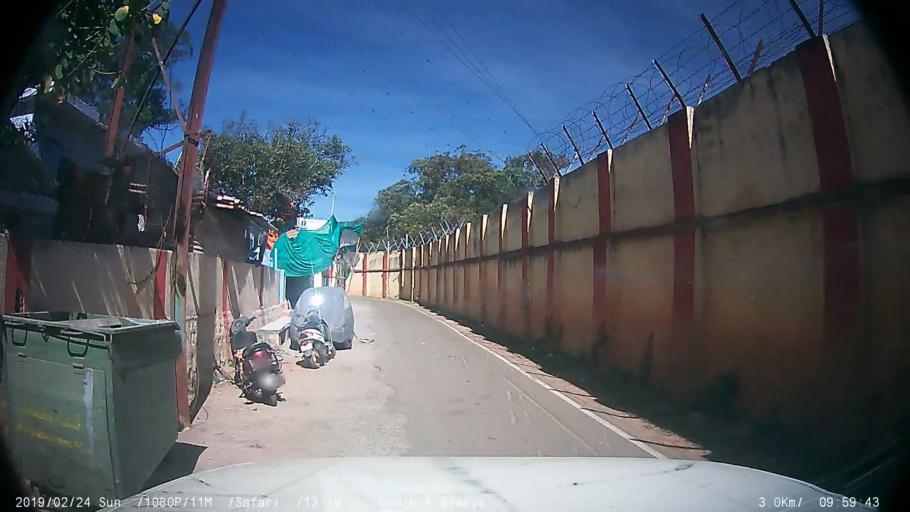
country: IN
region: Tamil Nadu
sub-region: Nilgiri
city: Aravankadu
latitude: 11.3622
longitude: 76.7661
